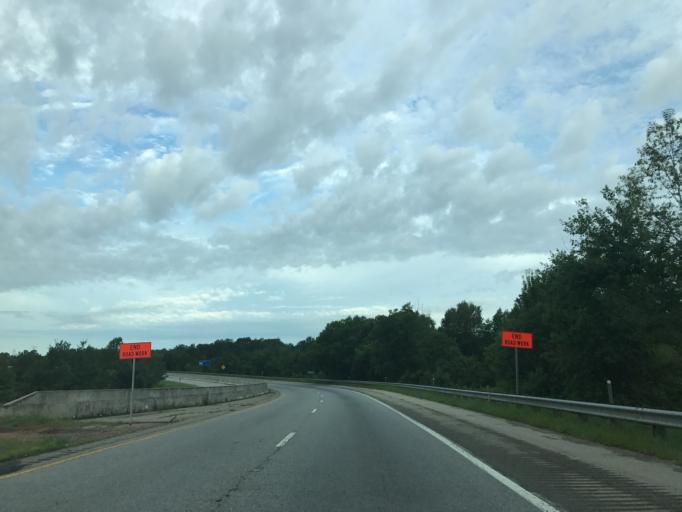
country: US
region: South Carolina
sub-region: Spartanburg County
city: Valley Falls
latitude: 35.0130
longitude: -81.9101
